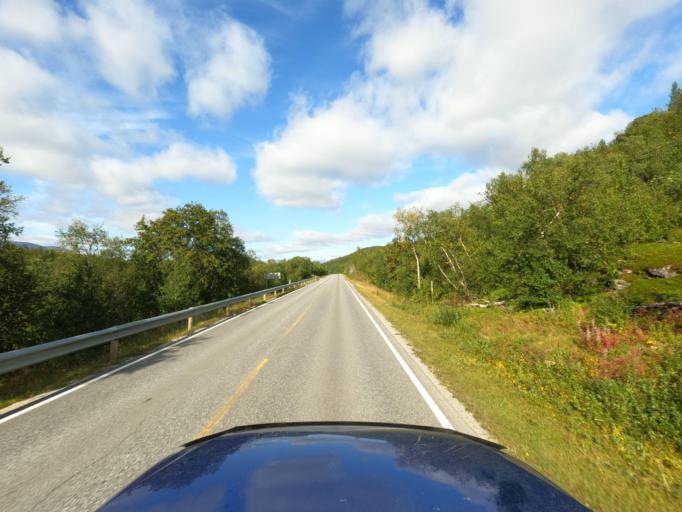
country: NO
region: Finnmark Fylke
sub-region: Porsanger
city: Lakselv
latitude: 69.9345
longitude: 24.9758
